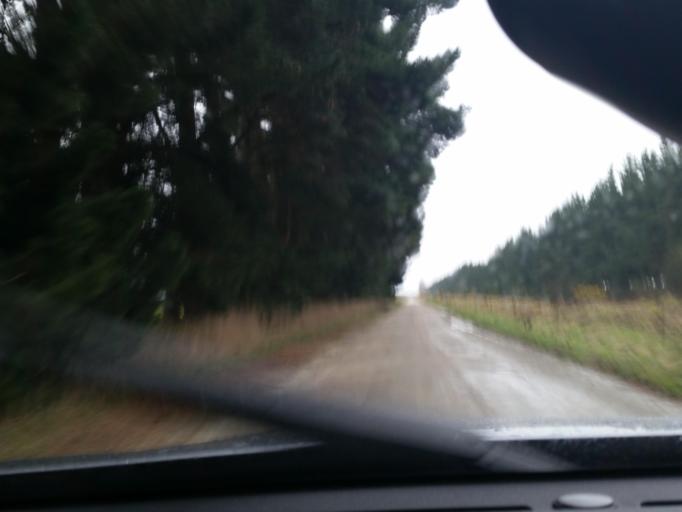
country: NZ
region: Southland
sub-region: Southland District
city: Winton
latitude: -46.2206
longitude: 168.4942
